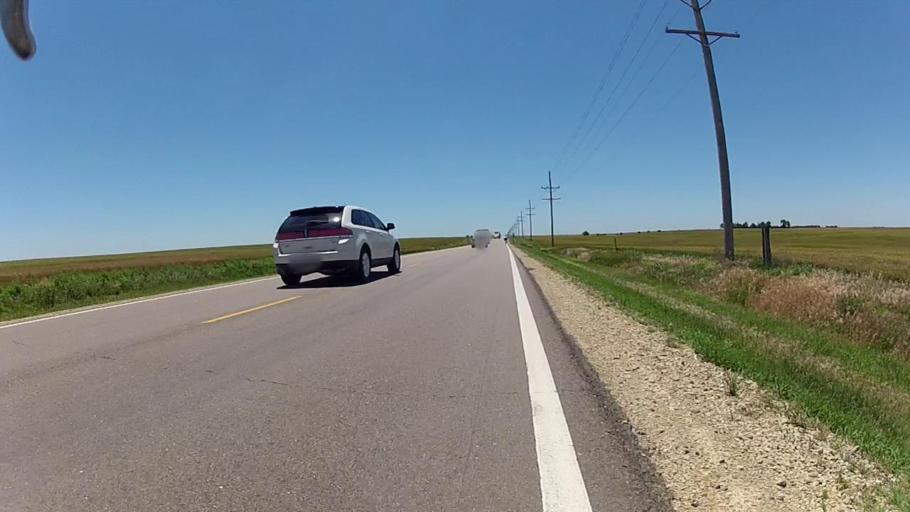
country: US
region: Kansas
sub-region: Kiowa County
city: Greensburg
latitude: 37.5326
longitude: -99.3208
